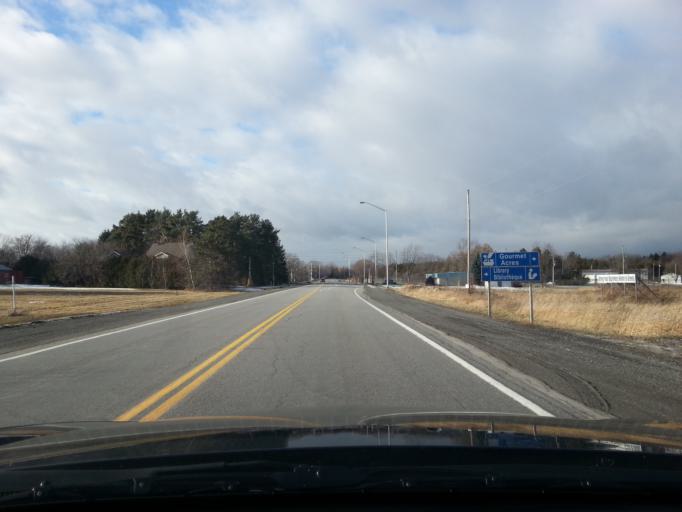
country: CA
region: Ontario
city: Ottawa
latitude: 45.2628
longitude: -75.5549
